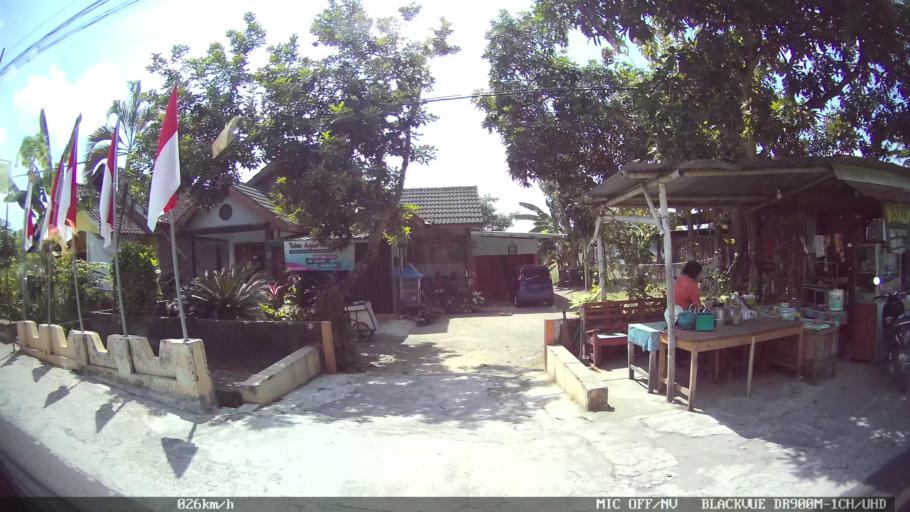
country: ID
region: Daerah Istimewa Yogyakarta
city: Sewon
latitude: -7.8391
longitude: 110.3815
